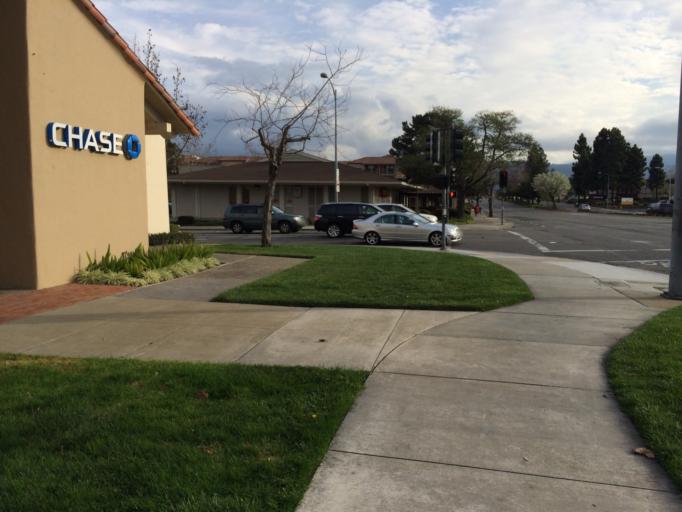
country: US
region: California
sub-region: Santa Clara County
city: Cupertino
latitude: 37.3196
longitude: -122.0321
